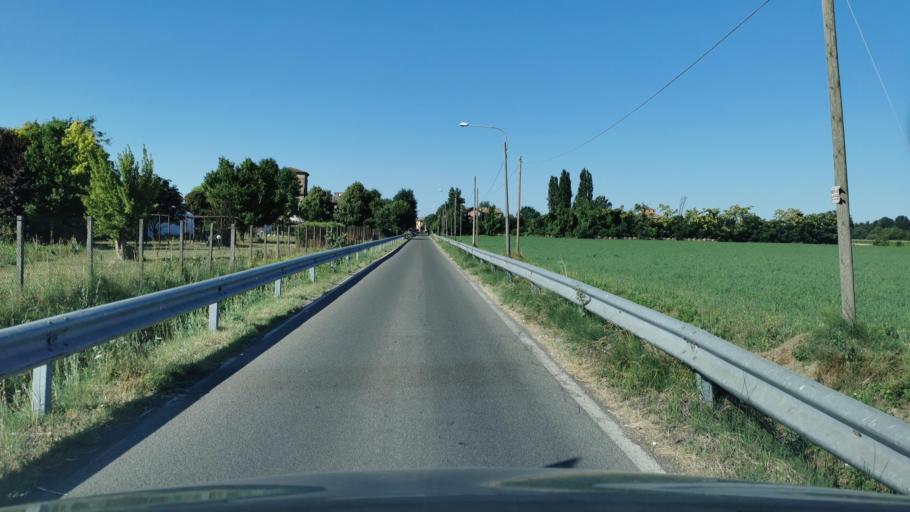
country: IT
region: Emilia-Romagna
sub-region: Provincia di Modena
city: Modena
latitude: 44.6221
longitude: 10.9066
